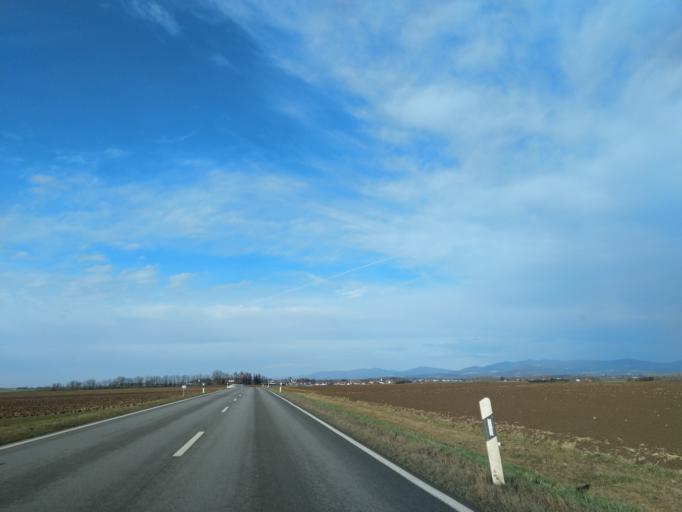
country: DE
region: Bavaria
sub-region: Lower Bavaria
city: Osterhofen
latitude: 48.6694
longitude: 13.0362
